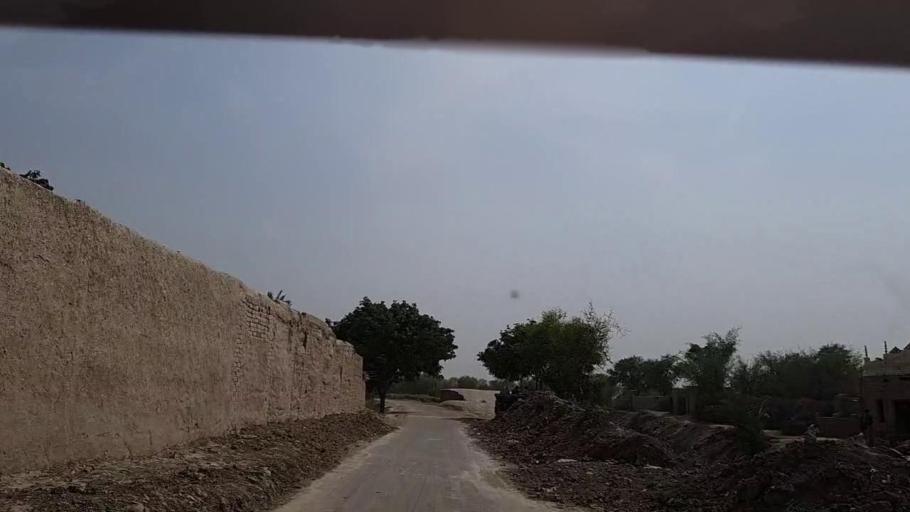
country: PK
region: Sindh
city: Khairpur Nathan Shah
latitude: 27.0533
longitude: 67.6836
